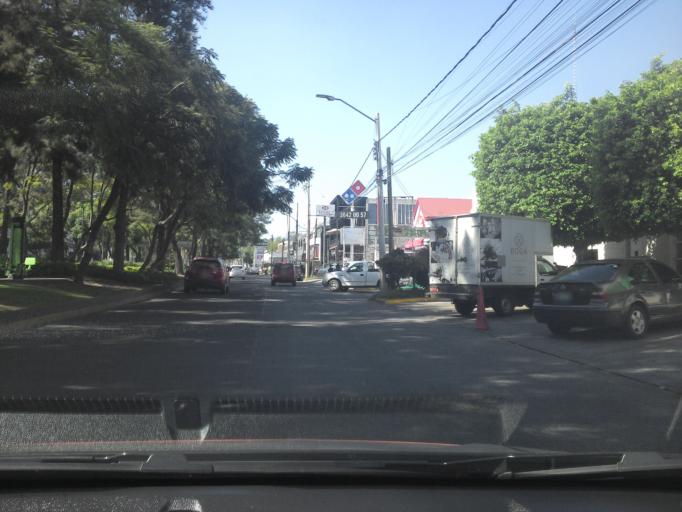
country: MX
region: Jalisco
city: Zapopan2
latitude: 20.6980
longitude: -103.3867
